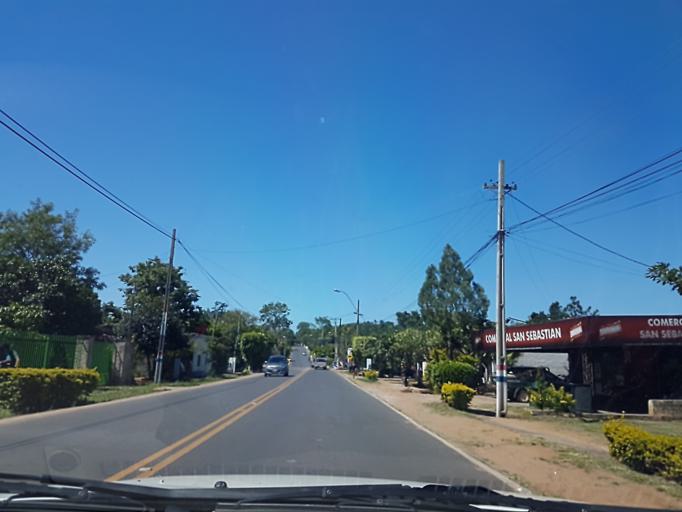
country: PY
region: Cordillera
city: Atyra
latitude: -25.2829
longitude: -57.1763
